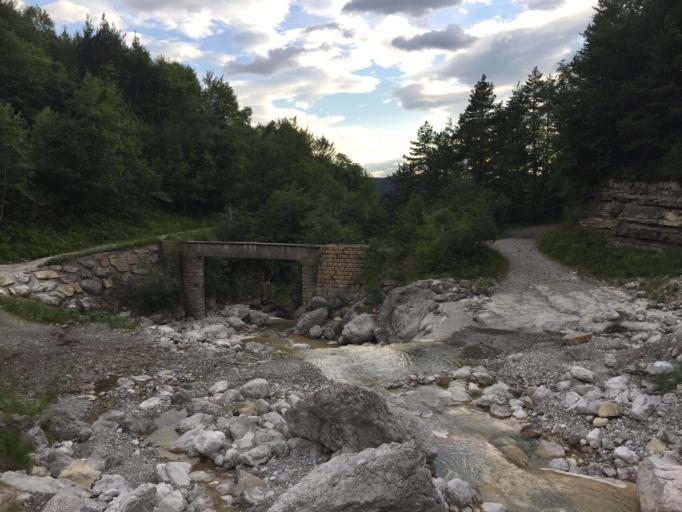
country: IT
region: Friuli Venezia Giulia
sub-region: Provincia di Udine
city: Paularo
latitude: 46.4696
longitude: 13.1076
